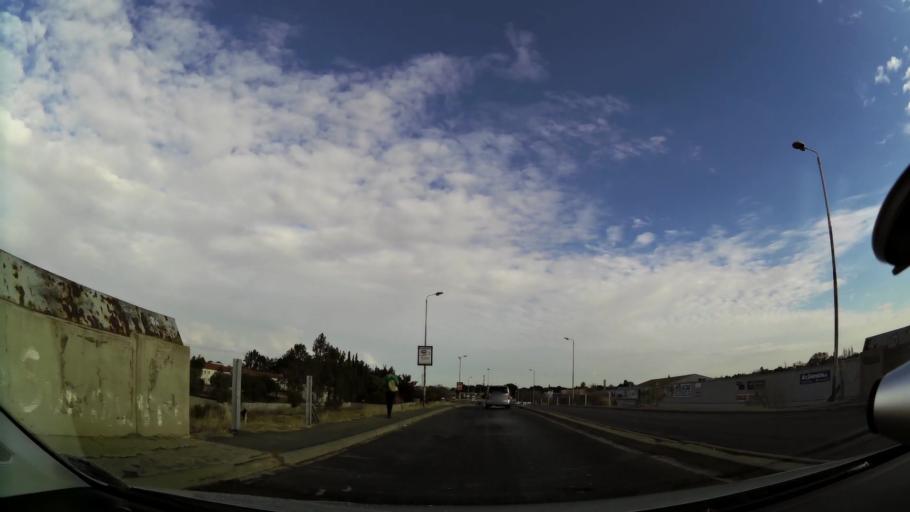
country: ZA
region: Orange Free State
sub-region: Lejweleputswa District Municipality
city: Welkom
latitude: -27.9776
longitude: 26.7621
